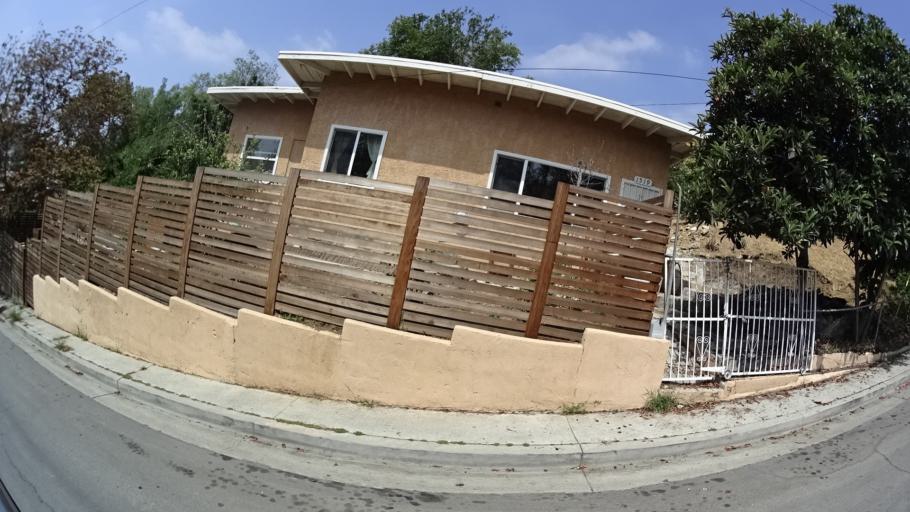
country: US
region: California
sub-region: Los Angeles County
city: Belvedere
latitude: 34.0587
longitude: -118.1694
